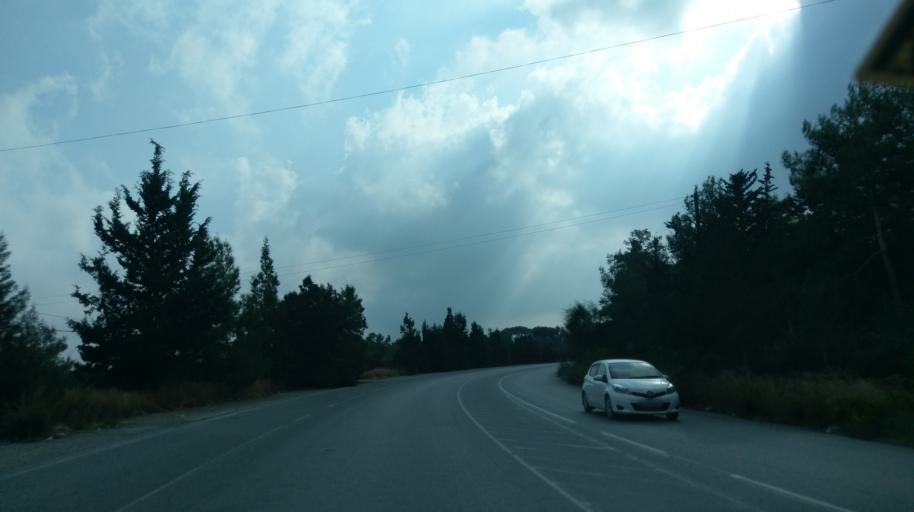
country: CY
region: Keryneia
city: Kyrenia
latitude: 35.3263
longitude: 33.4152
